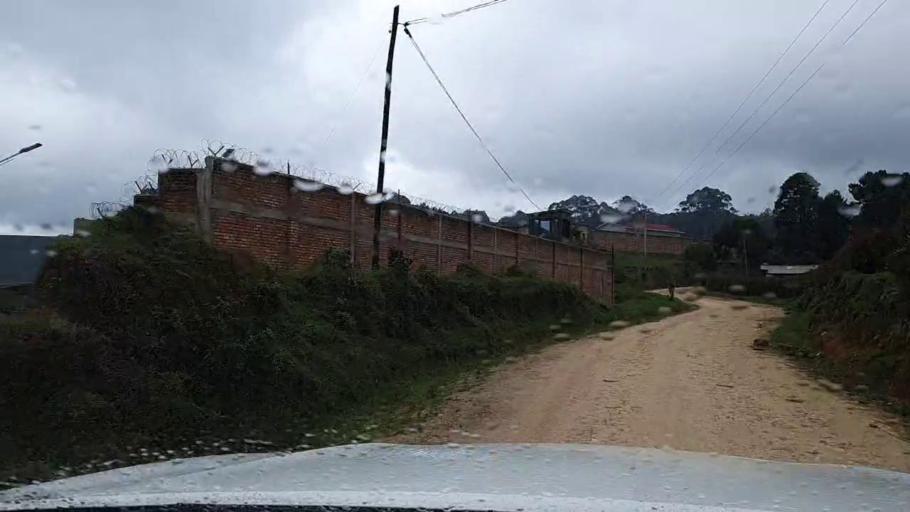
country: RW
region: Southern Province
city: Nzega
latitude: -2.3689
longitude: 29.3818
